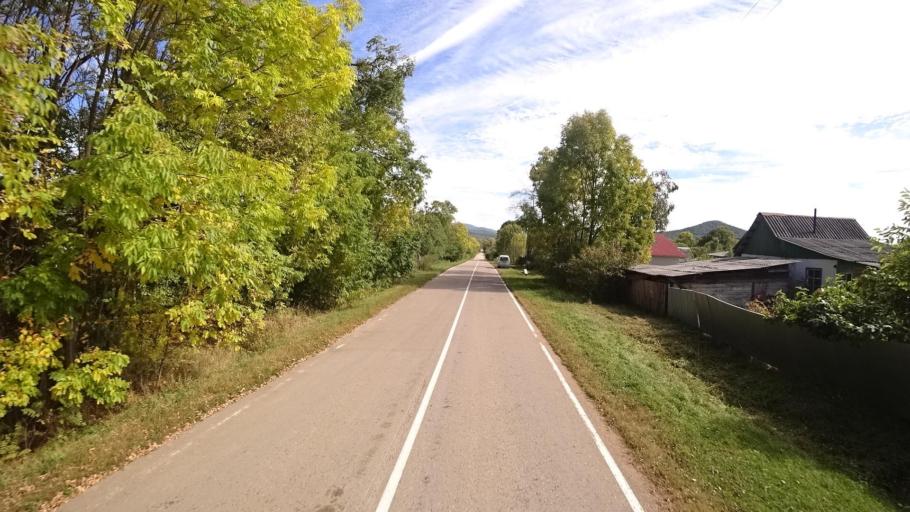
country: RU
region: Primorskiy
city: Yakovlevka
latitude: 44.3989
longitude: 133.5990
